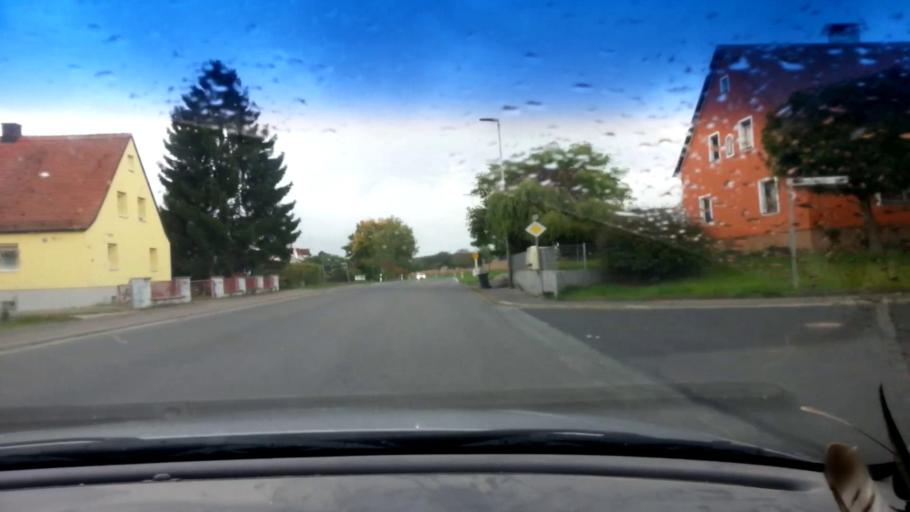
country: DE
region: Bavaria
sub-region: Upper Franconia
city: Stegaurach
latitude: 49.8654
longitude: 10.8358
